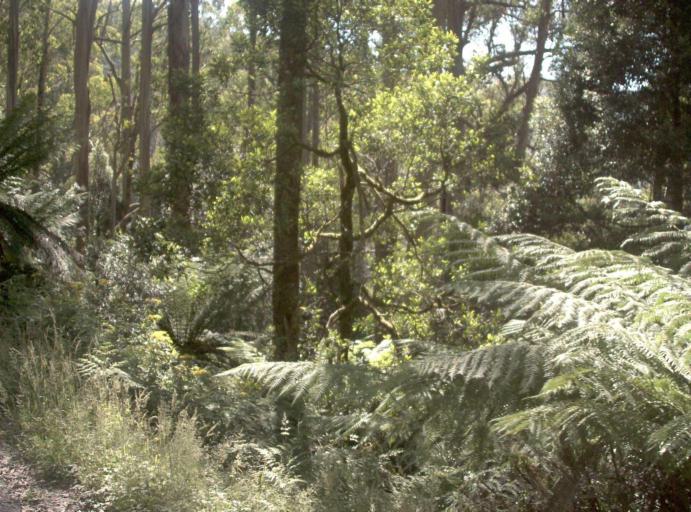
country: AU
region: Victoria
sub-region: Yarra Ranges
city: Millgrove
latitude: -37.7113
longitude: 145.6489
